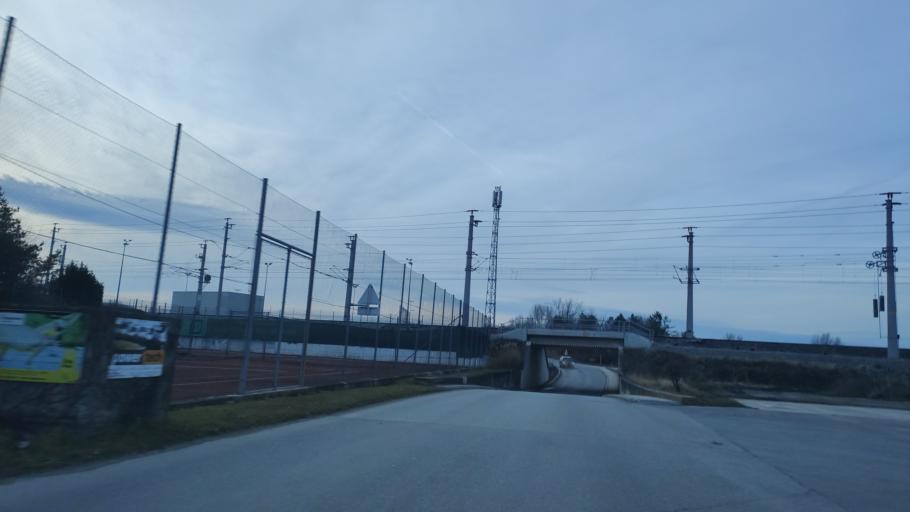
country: AT
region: Lower Austria
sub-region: Politischer Bezirk Wiener Neustadt
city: Lichtenworth
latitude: 47.8513
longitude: 16.3018
